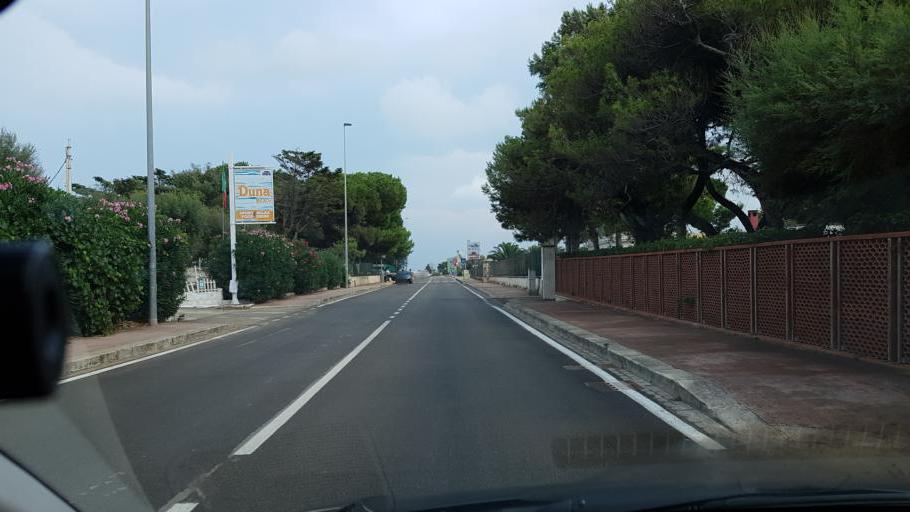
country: IT
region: Apulia
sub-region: Provincia di Brindisi
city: Fasano
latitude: 40.8982
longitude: 17.3650
